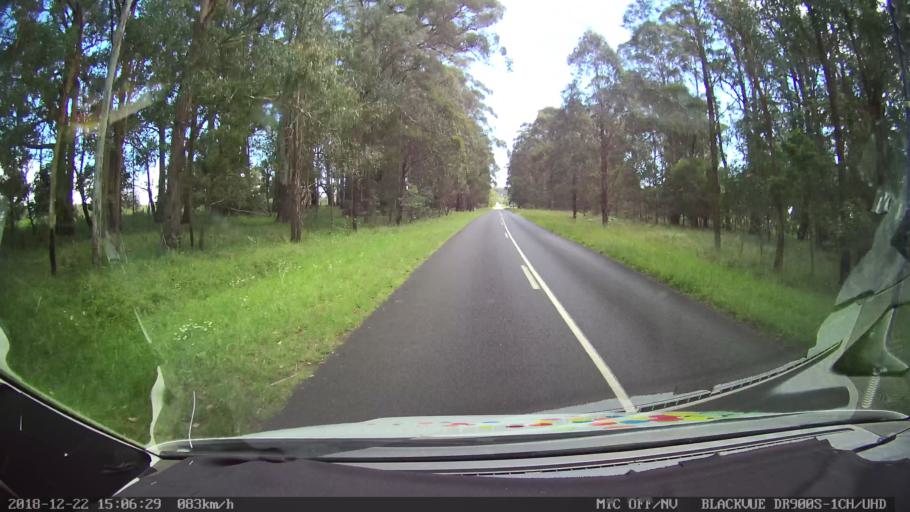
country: AU
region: New South Wales
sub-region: Bellingen
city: Dorrigo
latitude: -30.2939
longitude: 152.4268
